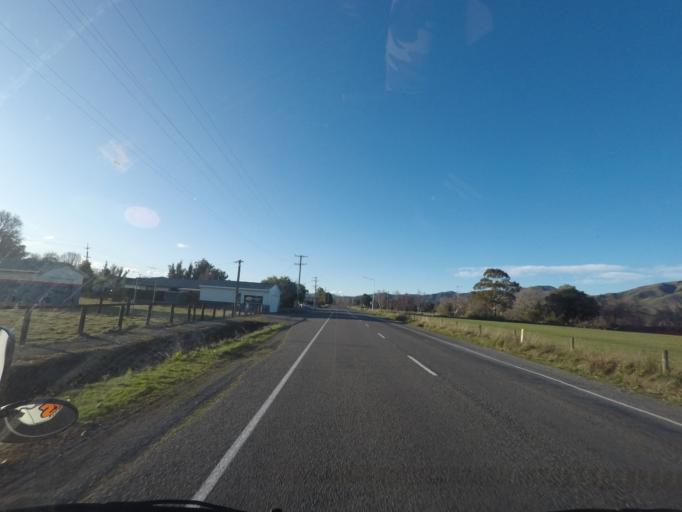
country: NZ
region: Canterbury
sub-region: Kaikoura District
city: Kaikoura
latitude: -42.7139
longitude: 173.2902
